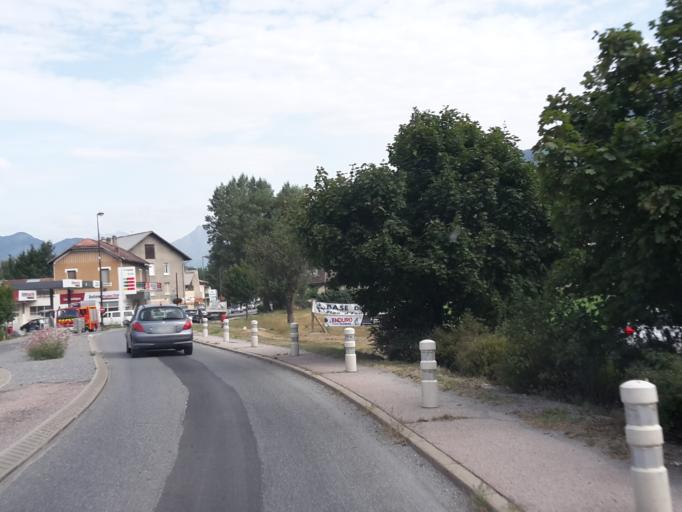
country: FR
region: Provence-Alpes-Cote d'Azur
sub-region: Departement des Hautes-Alpes
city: Guillestre
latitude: 44.6714
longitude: 6.6183
